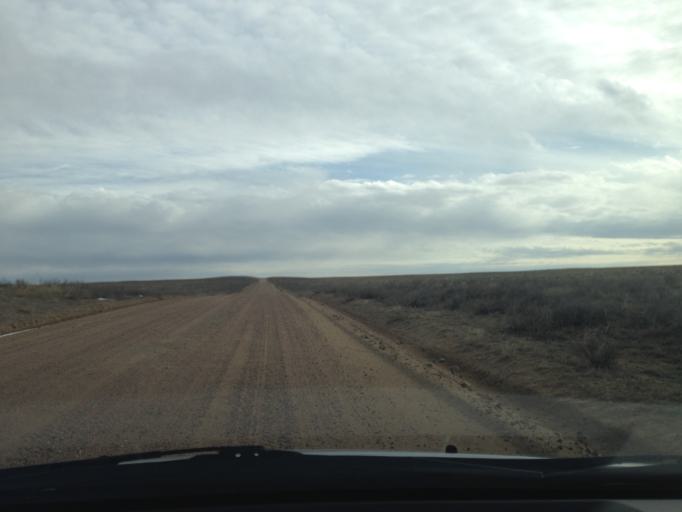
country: US
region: Colorado
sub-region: Weld County
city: Keenesburg
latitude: 40.2587
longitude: -104.2068
